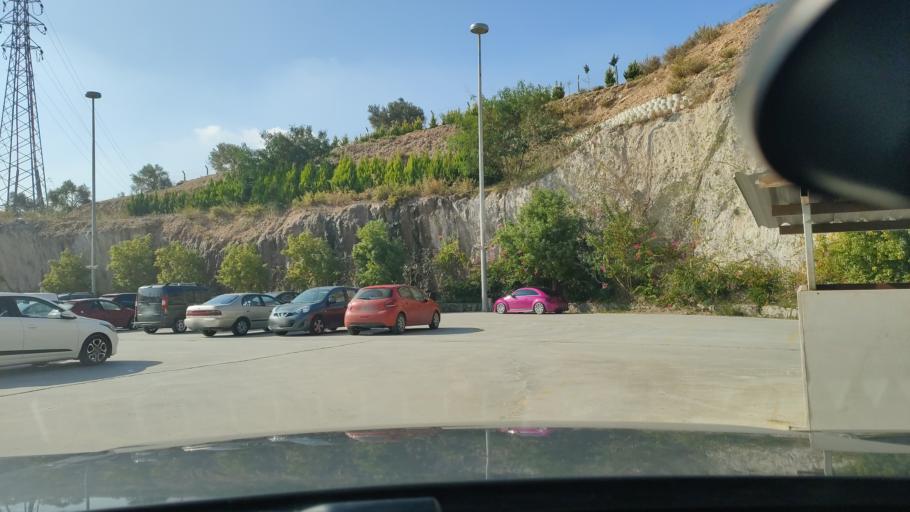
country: TR
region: Mugla
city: Ortakent
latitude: 37.0586
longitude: 27.3557
